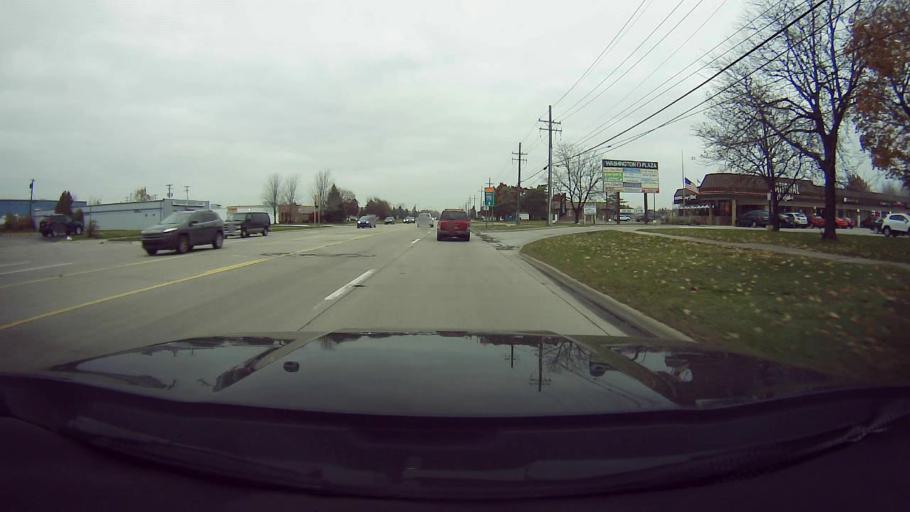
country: US
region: Michigan
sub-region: Oakland County
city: Madison Heights
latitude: 42.5356
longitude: -83.0868
